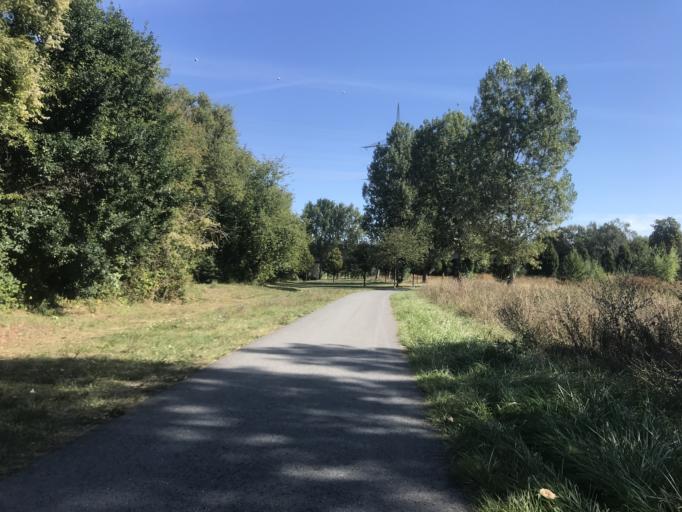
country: DE
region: Hesse
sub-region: Regierungsbezirk Darmstadt
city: Florsheim
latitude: 50.0030
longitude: 8.4207
